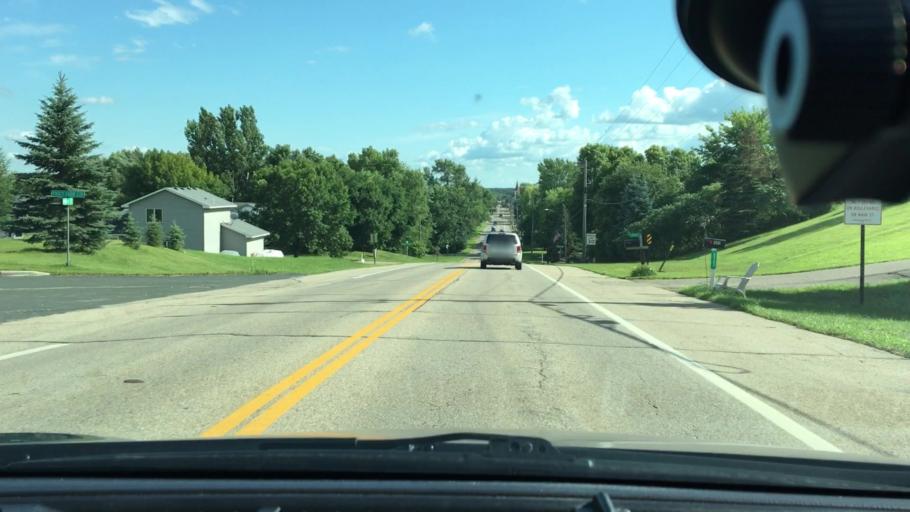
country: US
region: Minnesota
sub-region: Hennepin County
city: Saint Bonifacius
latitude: 44.9109
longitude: -93.7473
